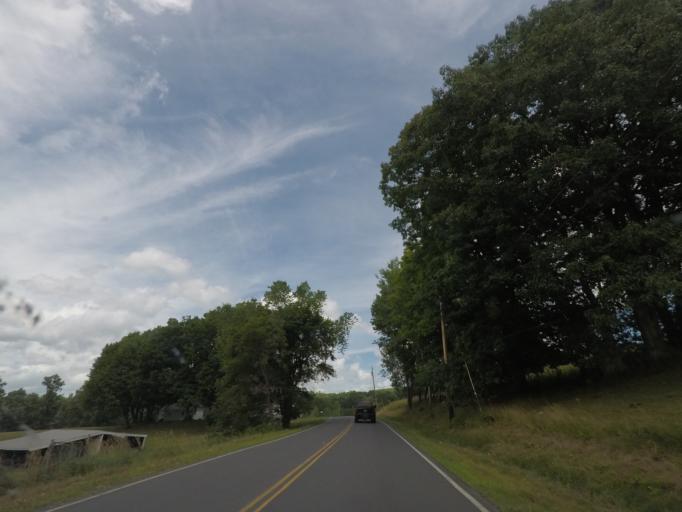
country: US
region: New York
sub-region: Rensselaer County
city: Wynantskill
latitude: 42.7024
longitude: -73.6175
